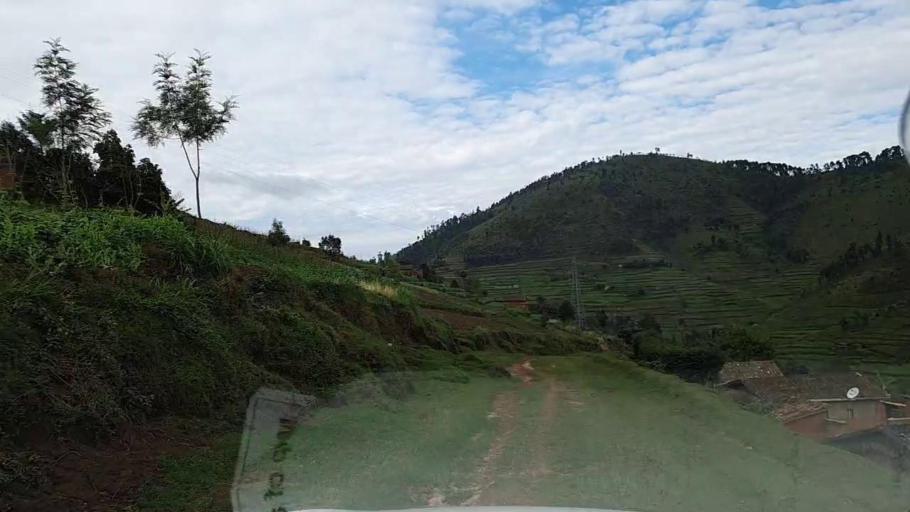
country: RW
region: Southern Province
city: Nzega
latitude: -2.4075
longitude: 29.4956
